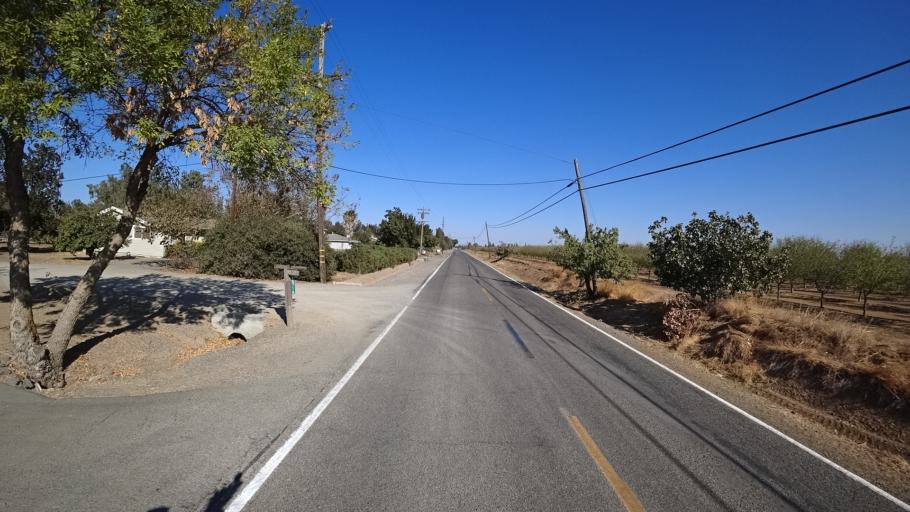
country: US
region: California
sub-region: Yolo County
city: Woodland
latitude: 38.6669
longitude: -121.8581
